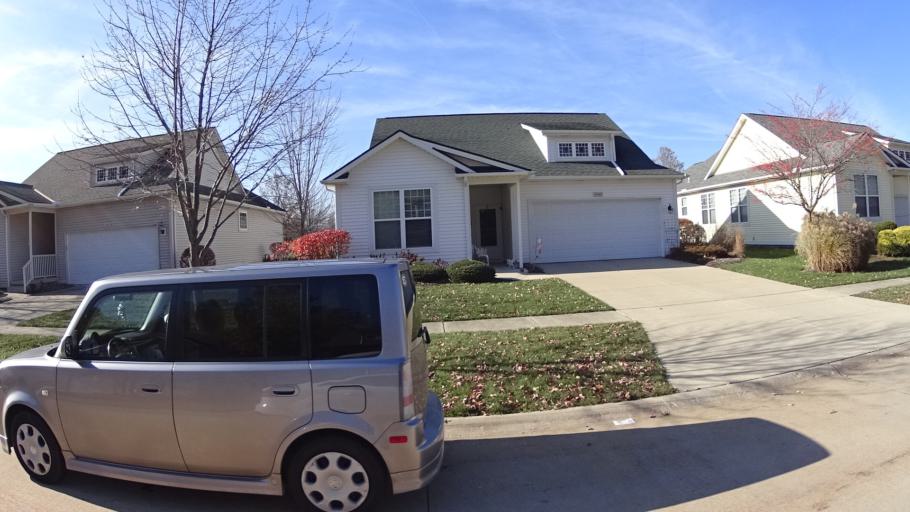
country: US
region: Ohio
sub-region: Lorain County
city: Avon Center
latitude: 41.4601
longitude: -82.0028
